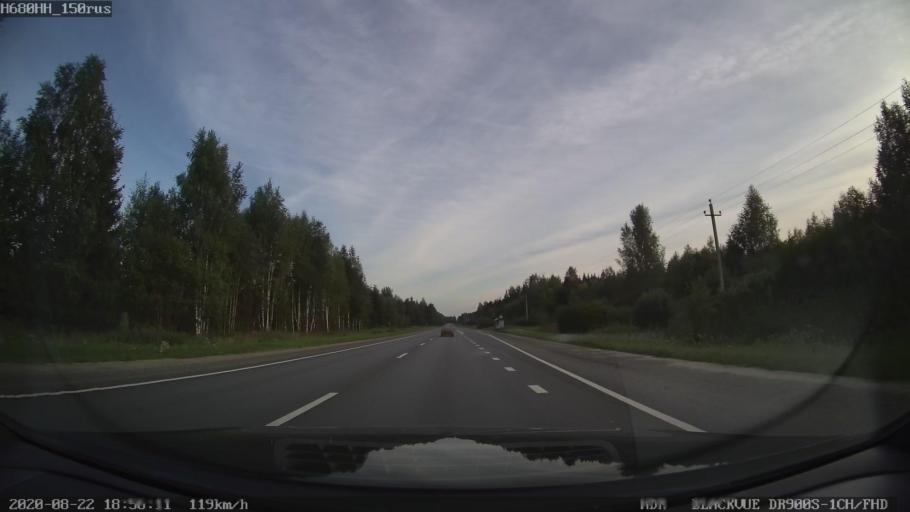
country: RU
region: Tverskaya
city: Rameshki
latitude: 57.1877
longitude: 36.0829
